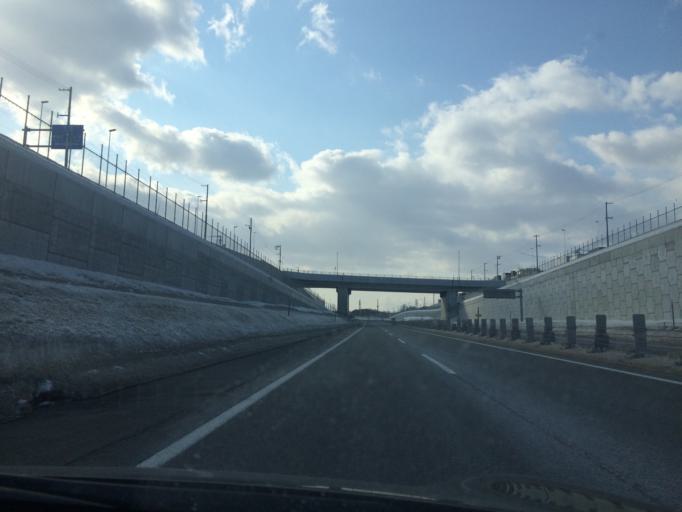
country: JP
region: Hokkaido
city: Kitahiroshima
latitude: 42.9944
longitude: 141.4691
